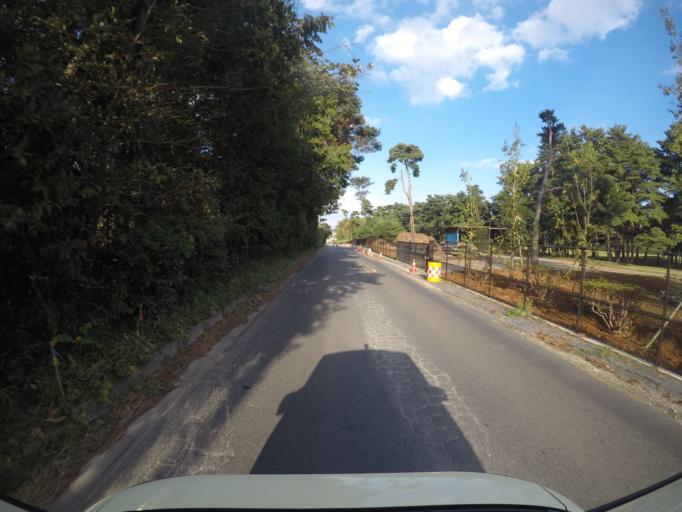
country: JP
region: Ibaraki
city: Mitsukaido
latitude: 36.0103
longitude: 140.0602
